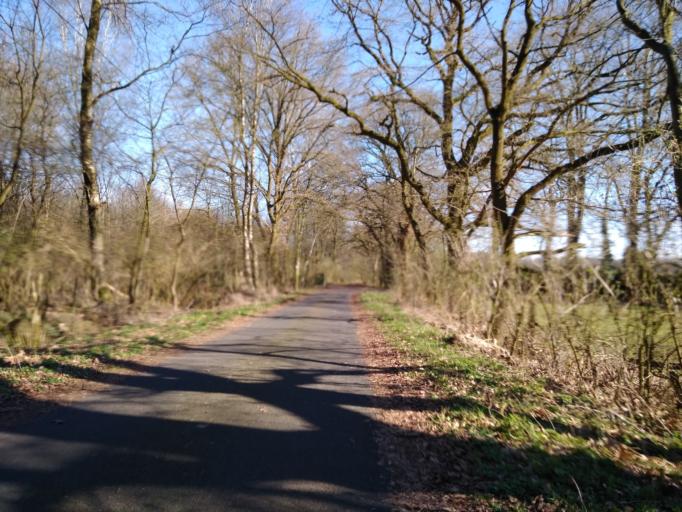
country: DE
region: North Rhine-Westphalia
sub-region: Regierungsbezirk Dusseldorf
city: Schermbeck
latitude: 51.6316
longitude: 6.8435
